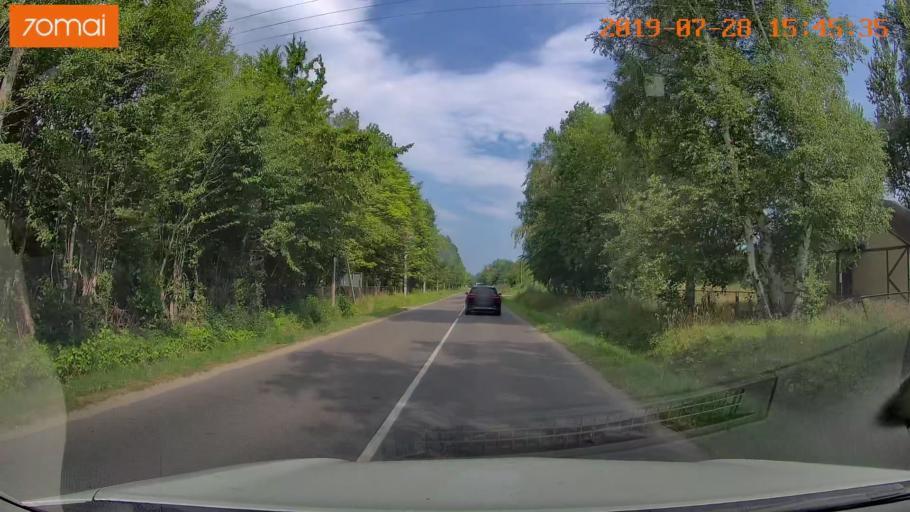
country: RU
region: Kaliningrad
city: Otradnoye
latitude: 54.9420
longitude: 20.0424
